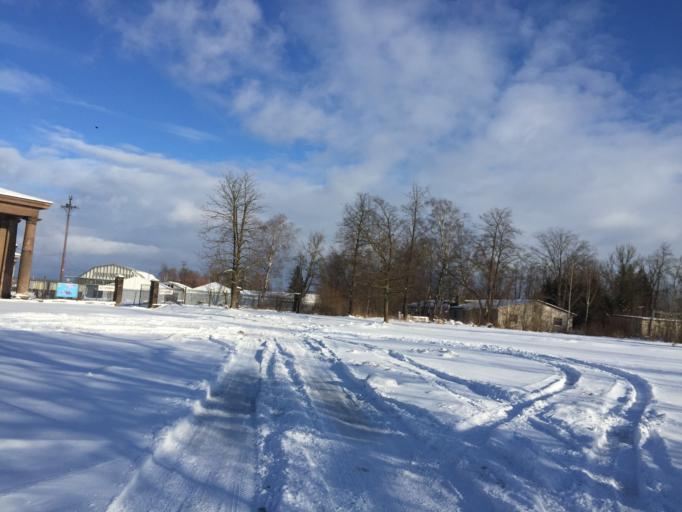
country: LV
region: Riga
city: Riga
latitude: 56.9755
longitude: 24.0729
